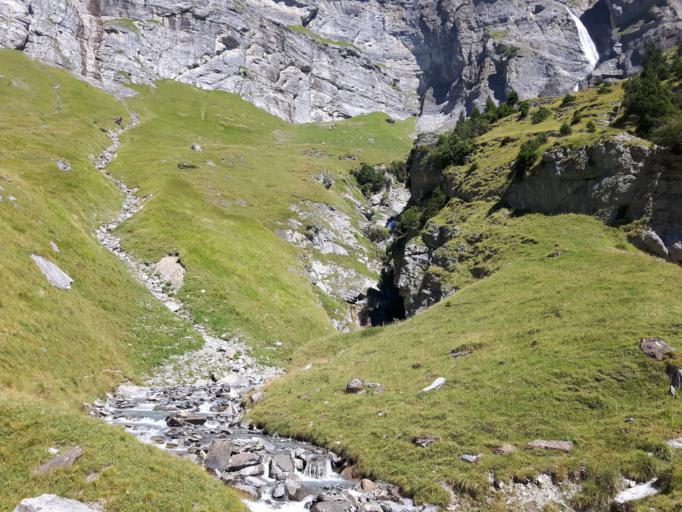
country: CH
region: Grisons
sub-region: Surselva District
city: Breil
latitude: 46.8360
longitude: 9.0993
